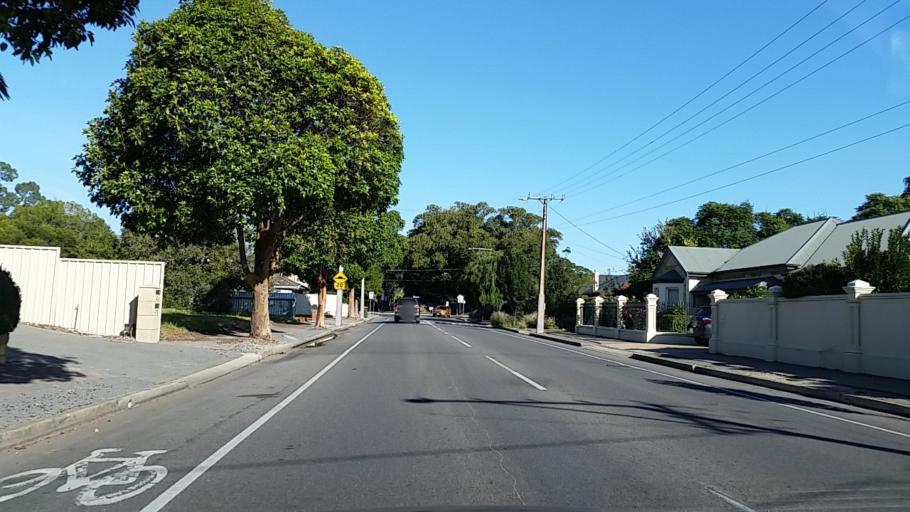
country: AU
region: South Australia
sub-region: Holdfast Bay
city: North Brighton
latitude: -34.9934
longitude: 138.5190
